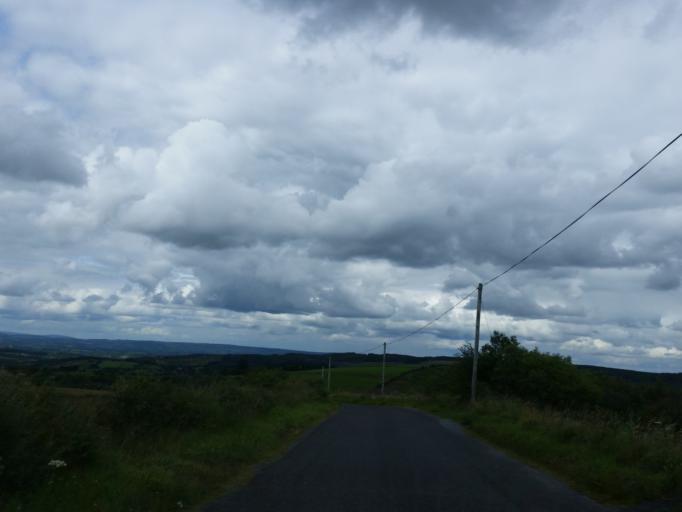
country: IE
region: Ulster
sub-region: County Monaghan
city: Clones
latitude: 54.2711
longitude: -7.2743
